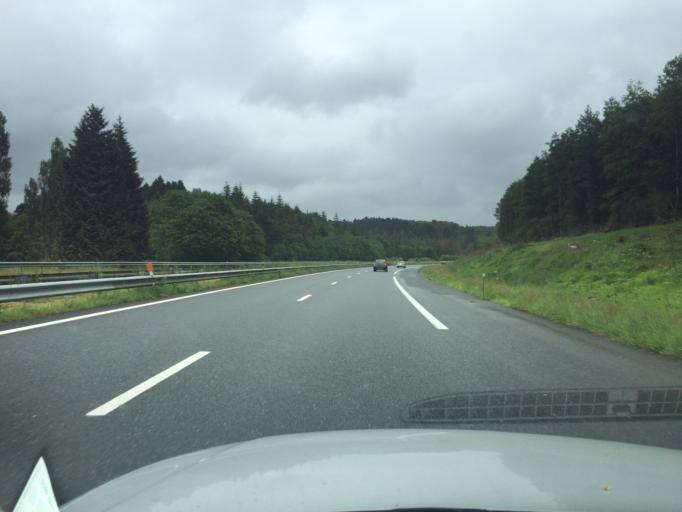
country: FR
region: Brittany
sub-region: Departement du Finistere
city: Plouigneau
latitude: 48.5776
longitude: -3.6517
